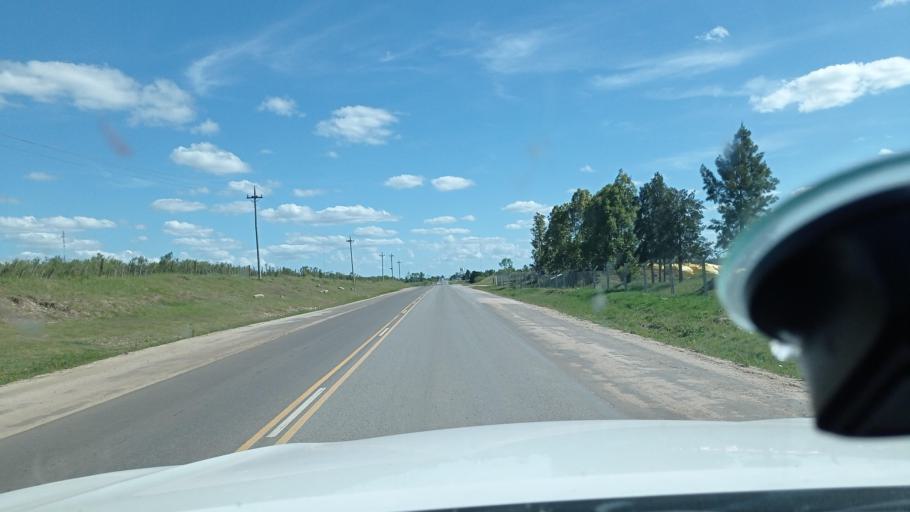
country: UY
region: Florida
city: Florida
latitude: -34.0772
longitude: -56.2345
